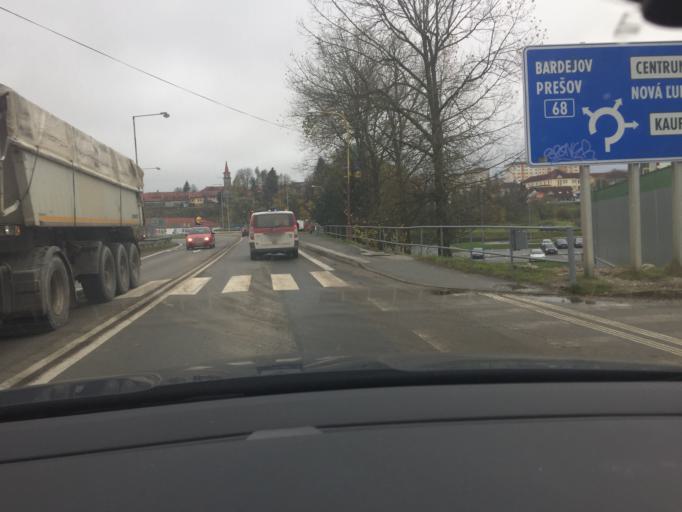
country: SK
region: Presovsky
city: Stara L'ubovna
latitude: 49.3063
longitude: 20.6866
